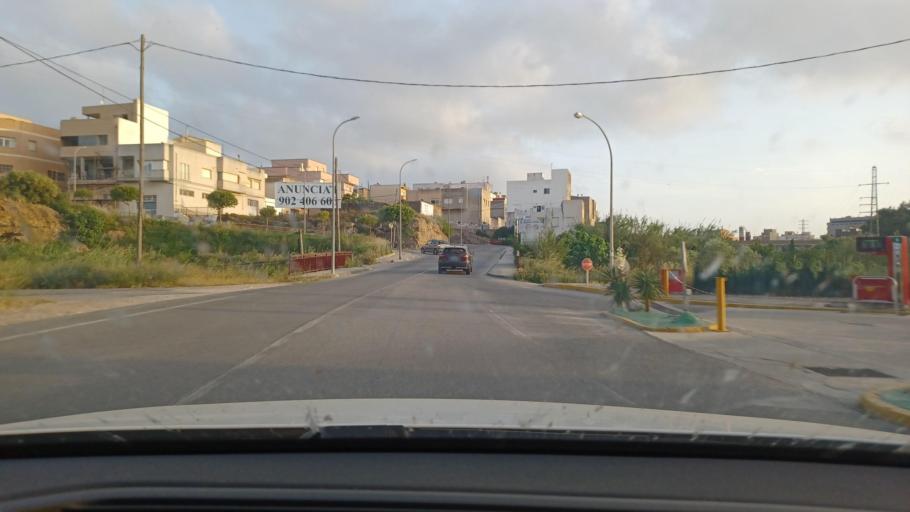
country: ES
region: Catalonia
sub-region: Provincia de Tarragona
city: Amposta
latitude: 40.7168
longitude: 0.5750
